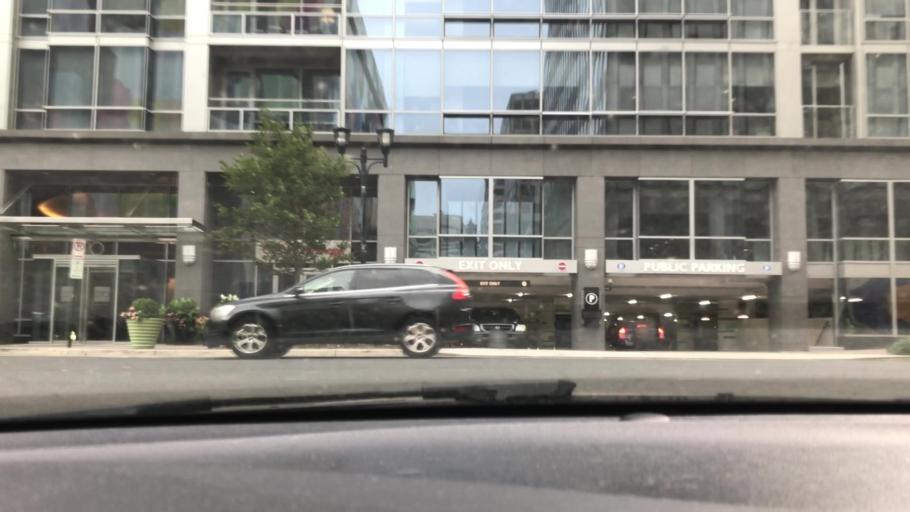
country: US
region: Washington, D.C.
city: Washington, D.C.
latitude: 38.8561
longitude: -77.0500
